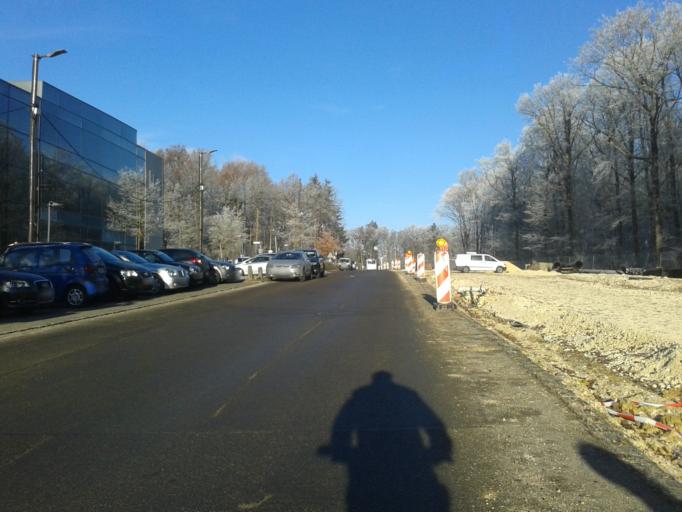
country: DE
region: Baden-Wuerttemberg
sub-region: Tuebingen Region
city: Ulm
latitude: 48.4236
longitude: 9.9580
